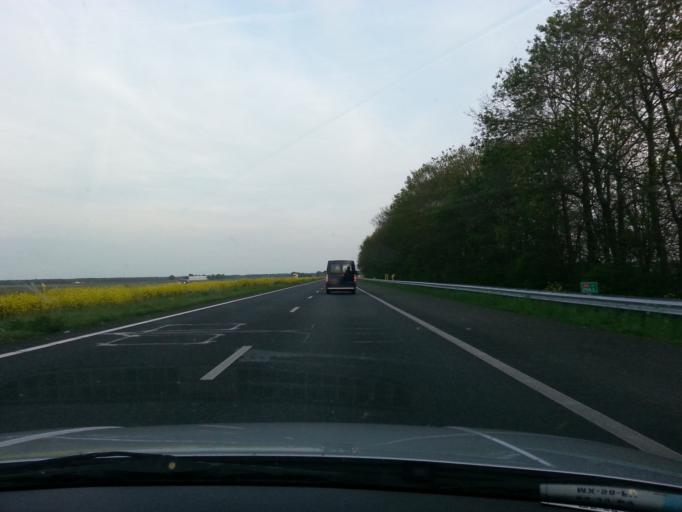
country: NL
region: Friesland
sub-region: Gemeente Lemsterland
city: Lemmer
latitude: 52.8265
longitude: 5.7365
